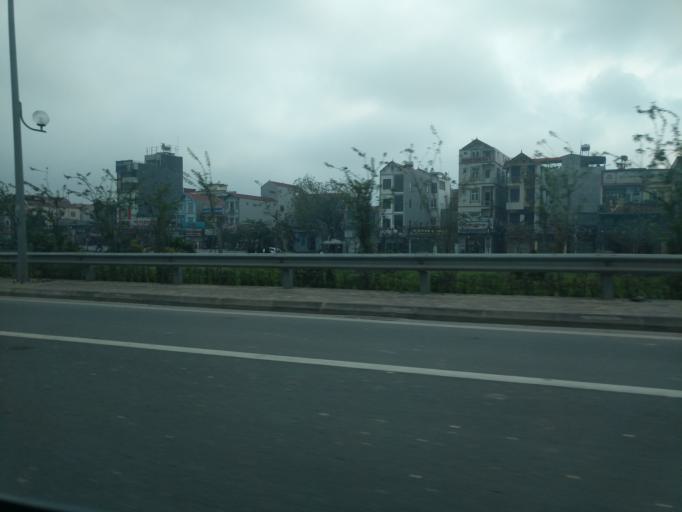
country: VN
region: Ha Noi
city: Dong Anh
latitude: 21.1149
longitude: 105.8273
